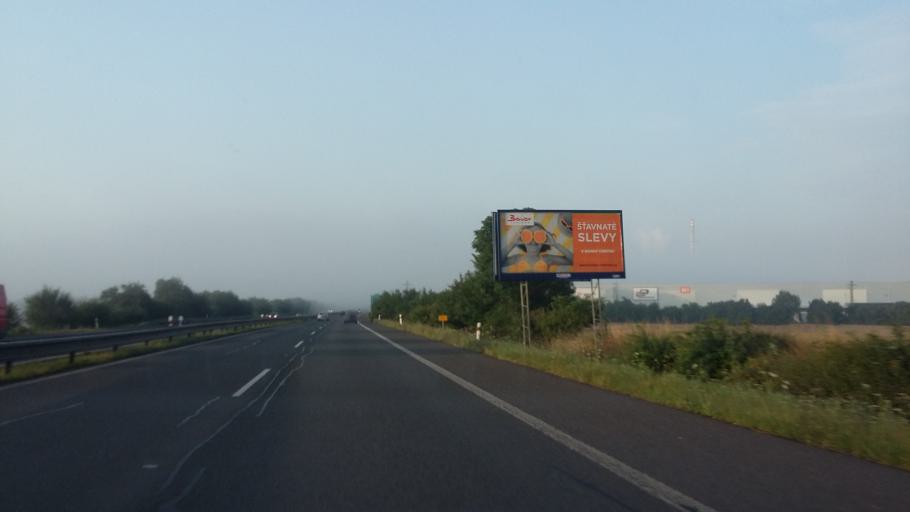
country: CZ
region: Central Bohemia
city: Kosmonosy
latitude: 50.4360
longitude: 14.9431
